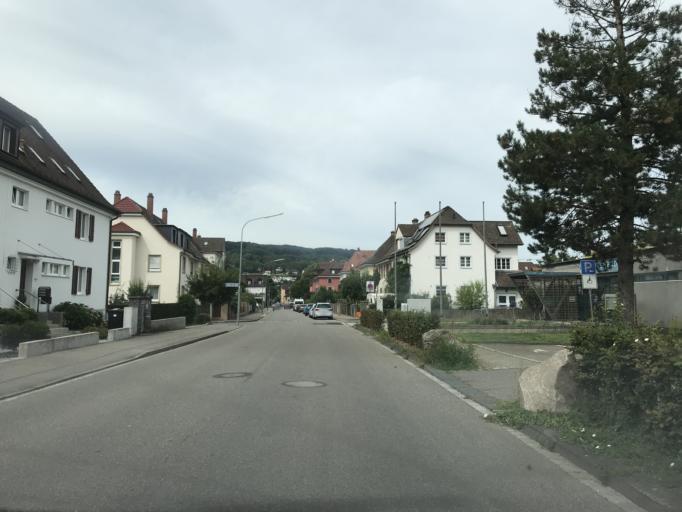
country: DE
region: Baden-Wuerttemberg
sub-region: Freiburg Region
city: Loerrach
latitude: 47.6060
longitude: 7.6653
